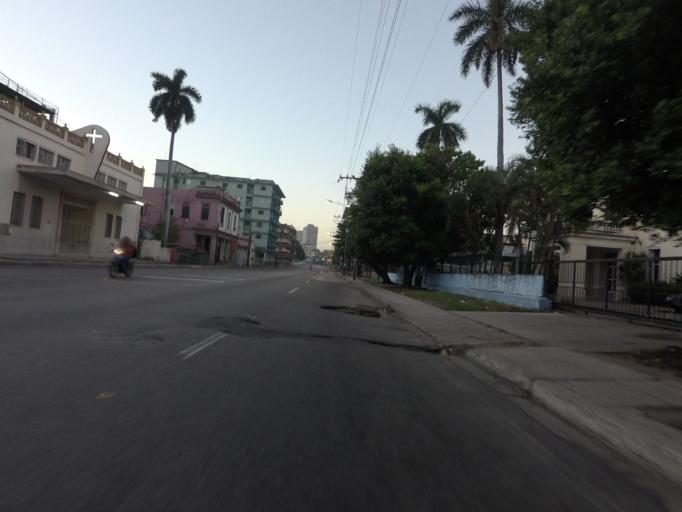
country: CU
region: La Habana
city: Havana
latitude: 23.1243
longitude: -82.3746
